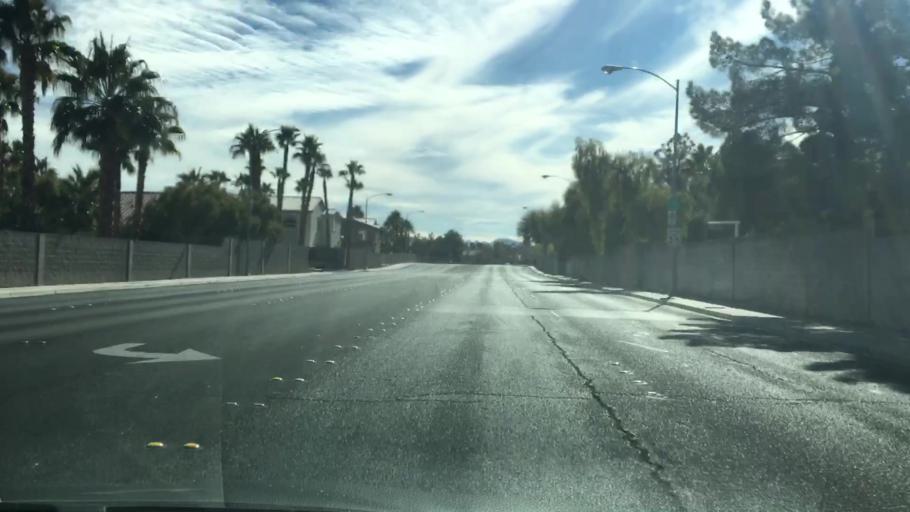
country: US
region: Nevada
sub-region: Clark County
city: Paradise
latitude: 36.0495
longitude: -115.1408
